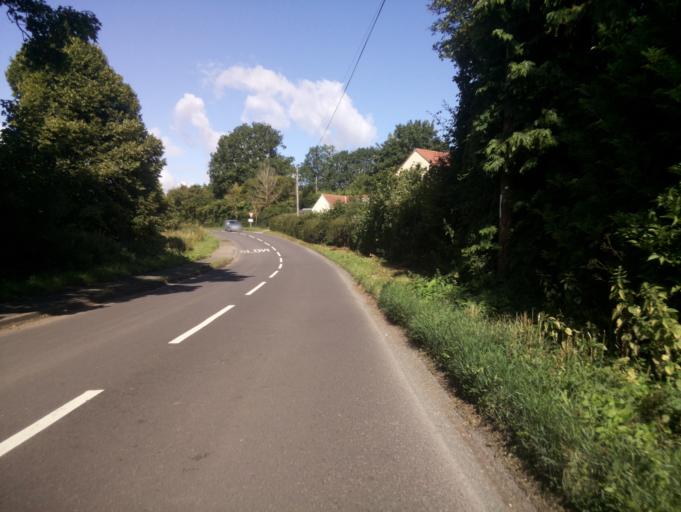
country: GB
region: England
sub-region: Herefordshire
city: Linton
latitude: 51.9399
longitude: -2.5226
